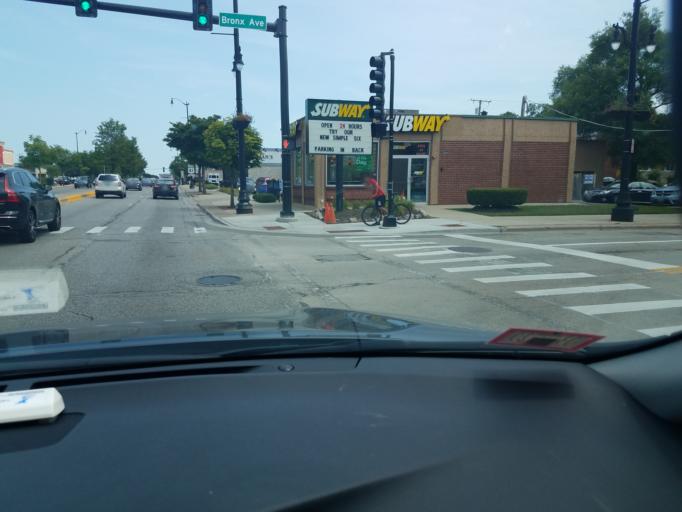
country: US
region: Illinois
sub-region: Cook County
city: Skokie
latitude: 42.0407
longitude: -87.7507
